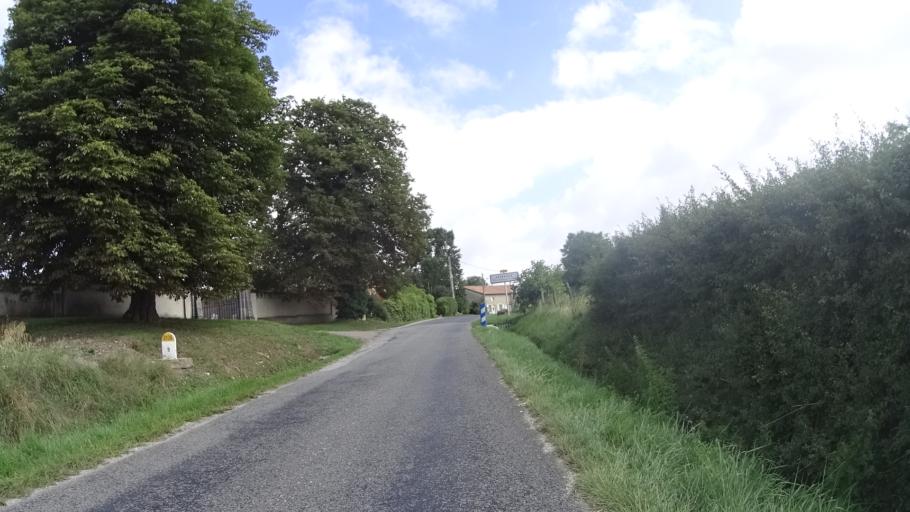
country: FR
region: Lorraine
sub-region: Departement de la Meuse
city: Ligny-en-Barrois
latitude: 48.7411
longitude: 5.3889
